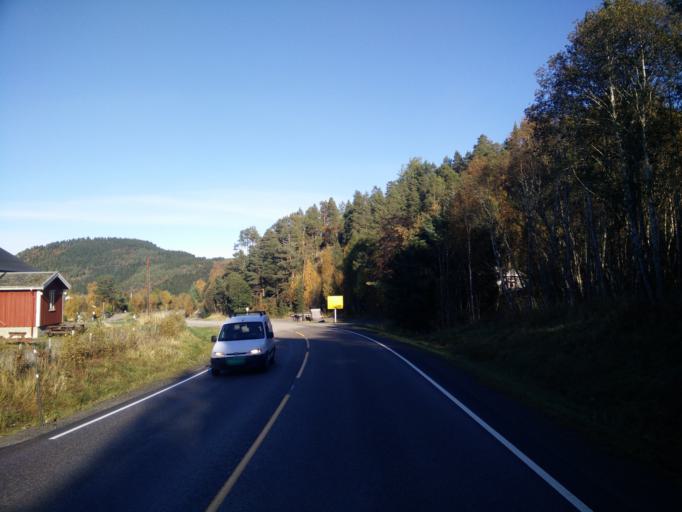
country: NO
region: More og Romsdal
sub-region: Kristiansund
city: Rensvik
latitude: 63.0135
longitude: 8.0022
